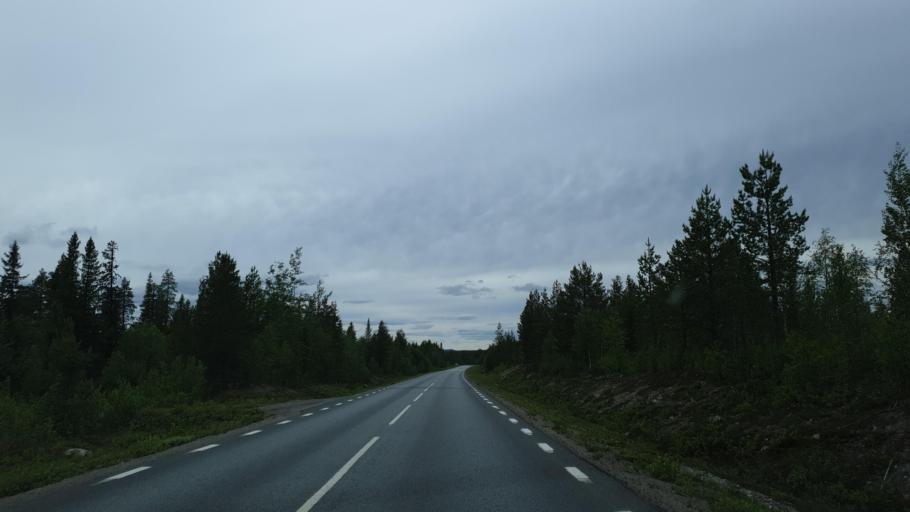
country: SE
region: Vaesterbotten
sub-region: Sorsele Kommun
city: Sorsele
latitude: 65.5151
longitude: 17.2017
